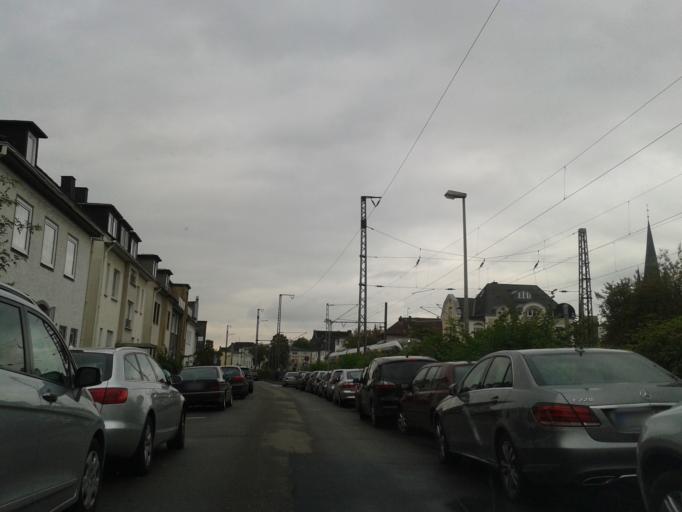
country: DE
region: North Rhine-Westphalia
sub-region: Regierungsbezirk Detmold
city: Paderborn
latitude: 51.7146
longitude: 8.7489
